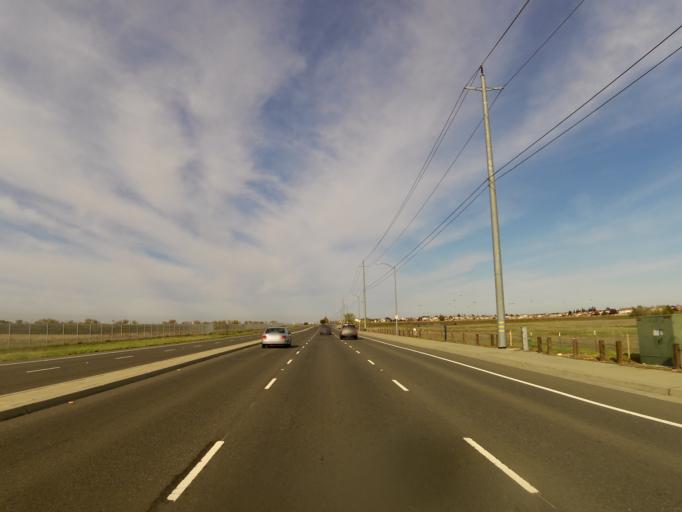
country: US
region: California
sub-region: Sacramento County
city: Rancho Cordova
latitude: 38.5323
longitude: -121.2429
